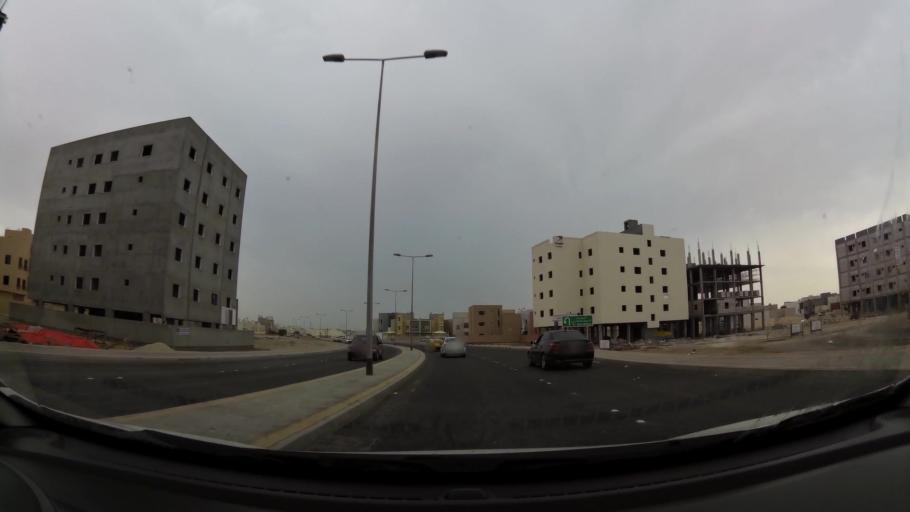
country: BH
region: Central Governorate
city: Madinat Hamad
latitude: 26.1298
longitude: 50.4892
